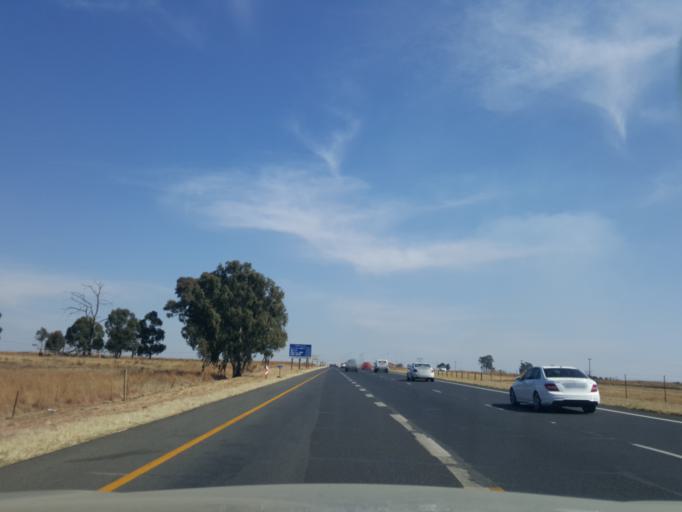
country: ZA
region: Mpumalanga
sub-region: Nkangala District Municipality
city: Middelburg
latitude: -25.8597
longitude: 29.3748
